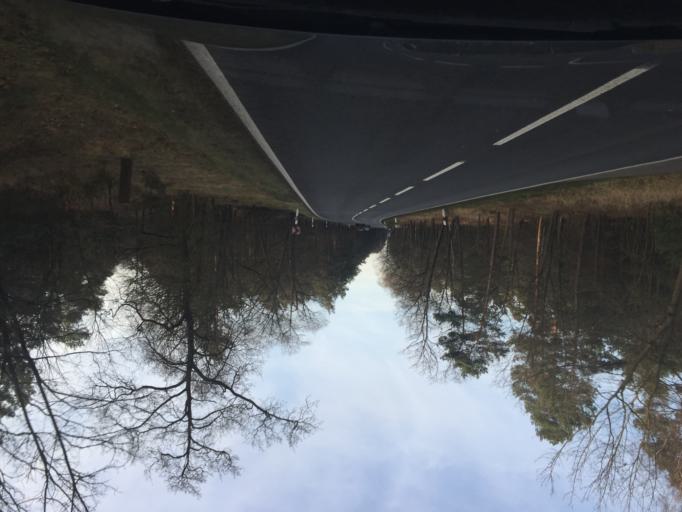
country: DE
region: Brandenburg
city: Cottbus
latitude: 51.7301
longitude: 14.4316
